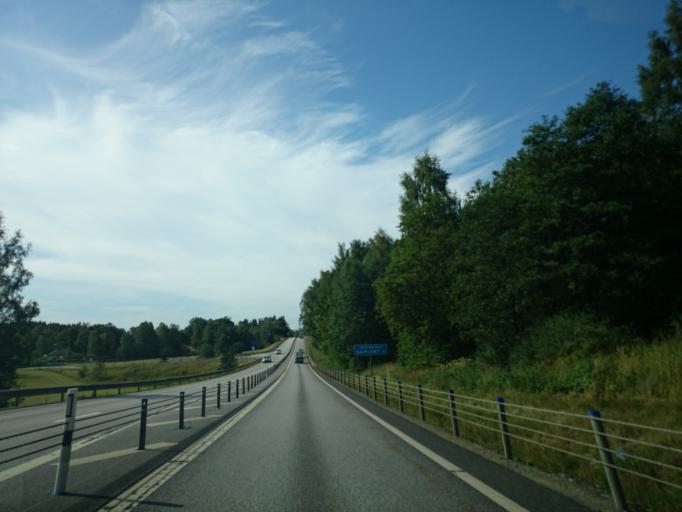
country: SE
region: Kalmar
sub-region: Vasterviks Kommun
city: Gamleby
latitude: 57.8930
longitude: 16.3868
